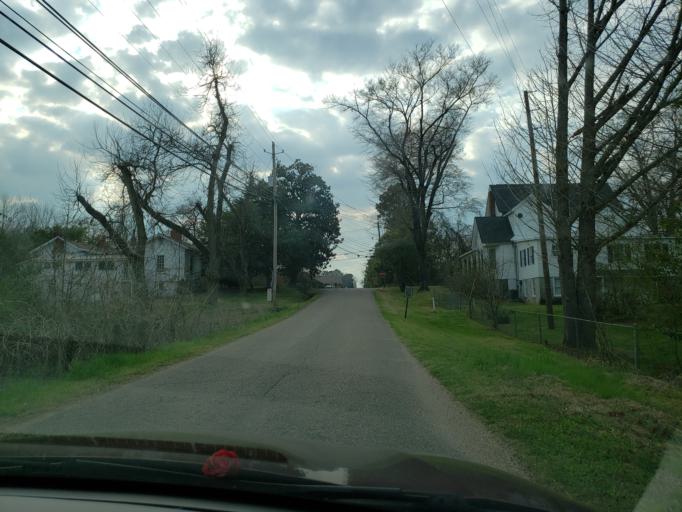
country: US
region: Alabama
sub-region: Hale County
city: Greensboro
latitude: 32.7029
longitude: -87.5976
